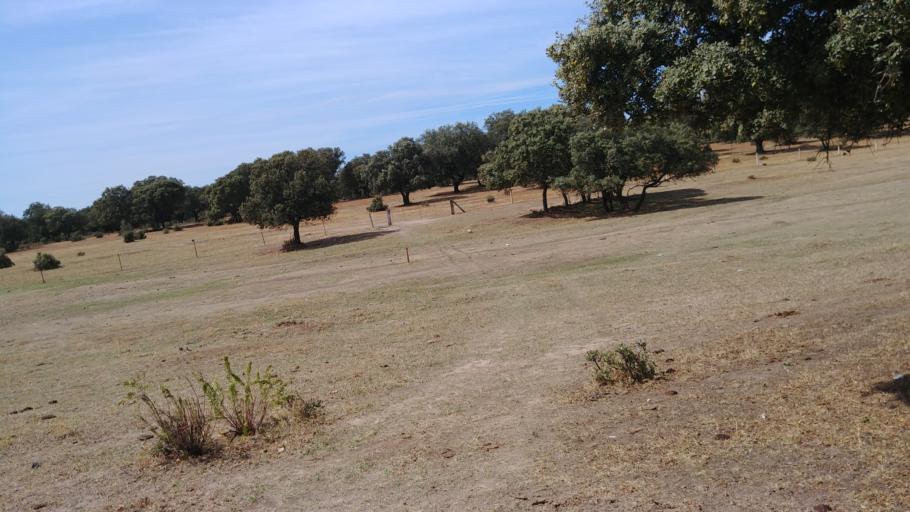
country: ES
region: Castille-La Mancha
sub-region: Province of Toledo
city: Navalcan
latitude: 40.0476
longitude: -5.1135
